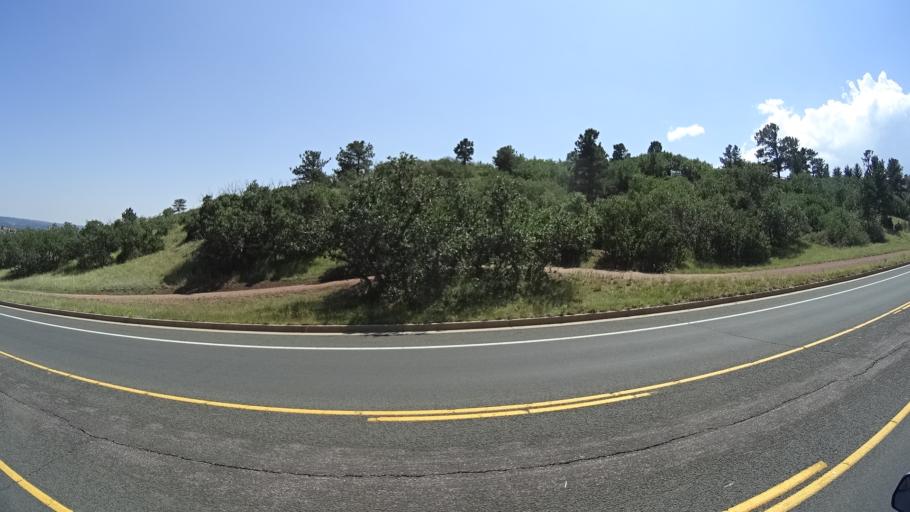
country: US
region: Colorado
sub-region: El Paso County
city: Manitou Springs
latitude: 38.9191
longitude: -104.8711
